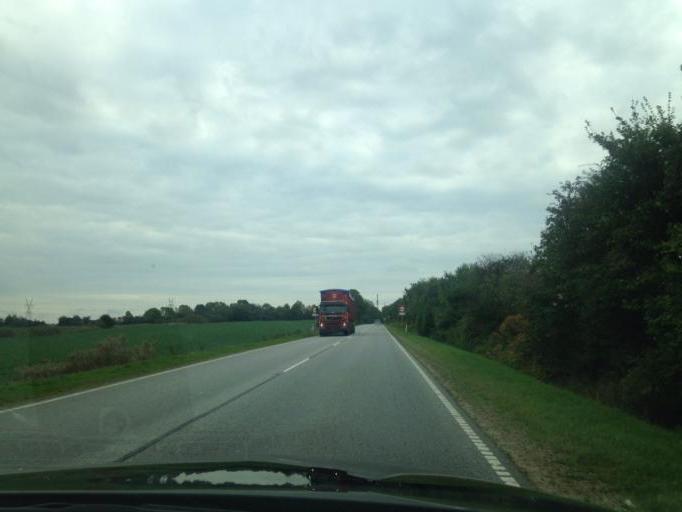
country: DK
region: South Denmark
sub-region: Haderslev Kommune
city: Vojens
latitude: 55.2557
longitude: 9.3364
